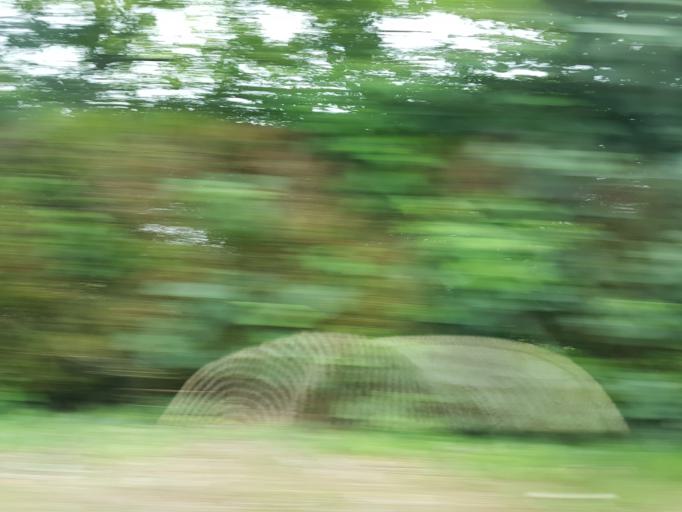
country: FR
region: Bourgogne
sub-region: Departement de la Nievre
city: Chateau-Chinon(Ville)
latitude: 47.0667
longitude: 3.9293
